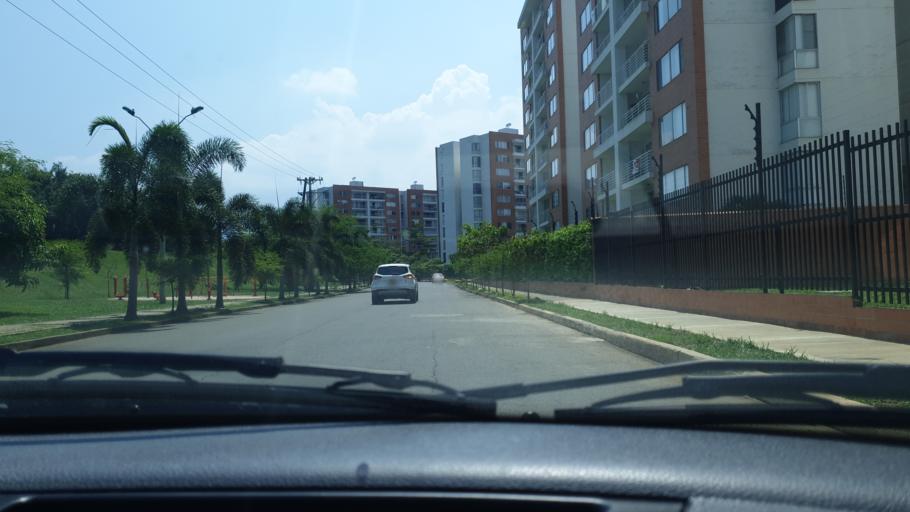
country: CO
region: Valle del Cauca
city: Cali
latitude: 3.3643
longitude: -76.5219
